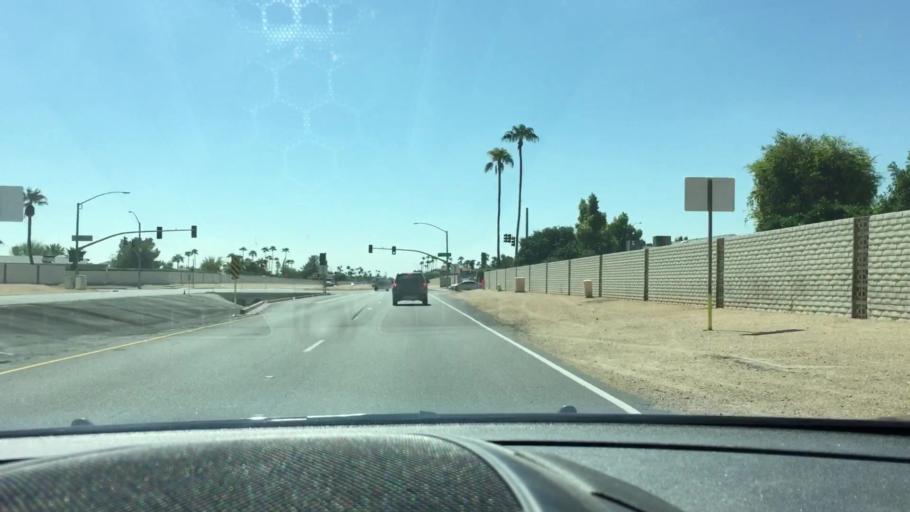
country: US
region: Arizona
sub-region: Maricopa County
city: Sun City
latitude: 33.6474
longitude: -112.2773
